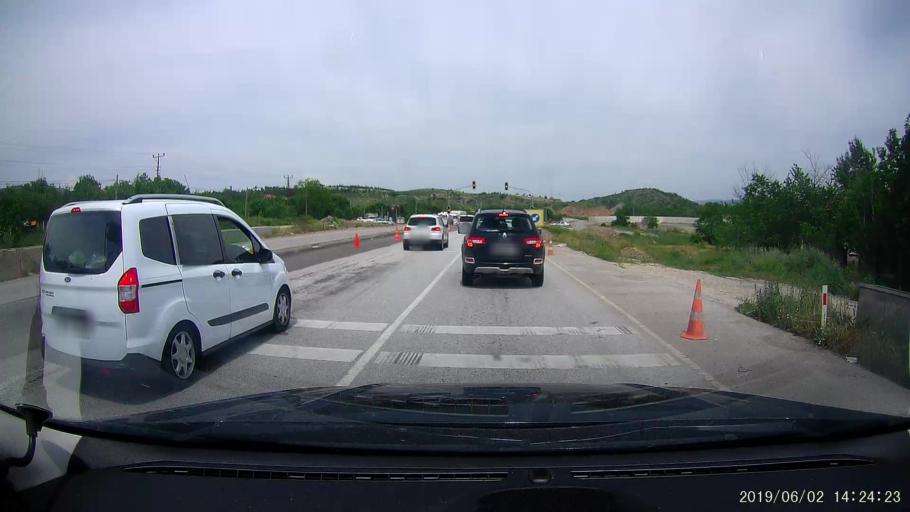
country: TR
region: Kastamonu
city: Tosya
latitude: 41.0011
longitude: 34.0302
